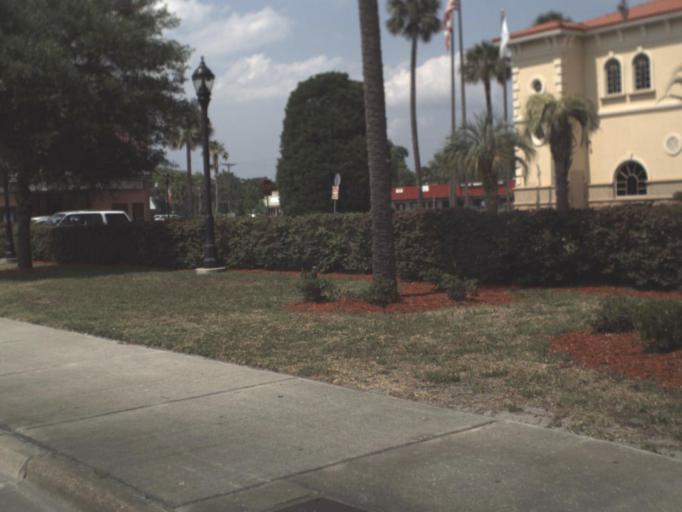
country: US
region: Florida
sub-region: Clay County
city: Green Cove Springs
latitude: 29.9930
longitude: -81.6792
